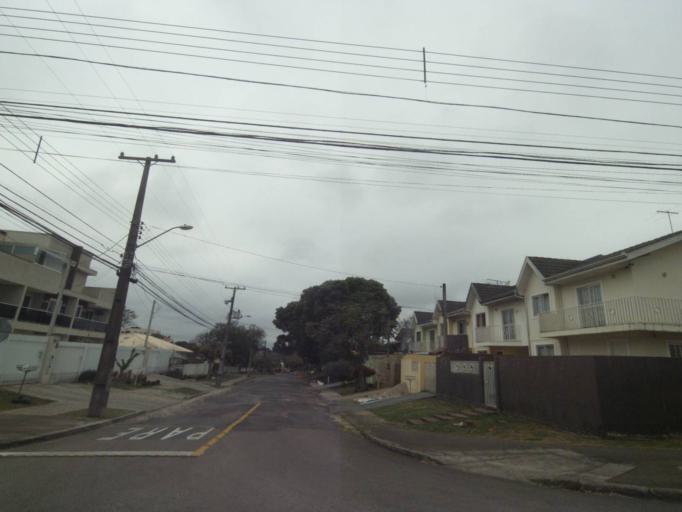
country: BR
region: Parana
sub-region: Pinhais
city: Pinhais
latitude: -25.4806
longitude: -49.2305
